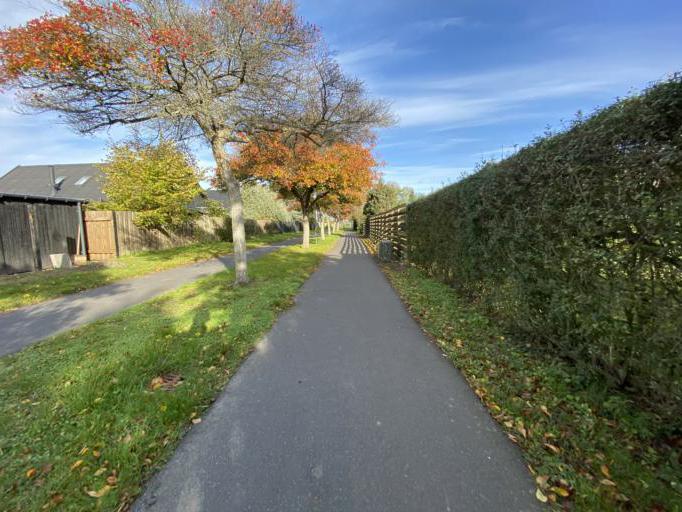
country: DK
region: Capital Region
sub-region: Dragor Kommune
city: Dragor
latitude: 55.5908
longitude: 12.6544
